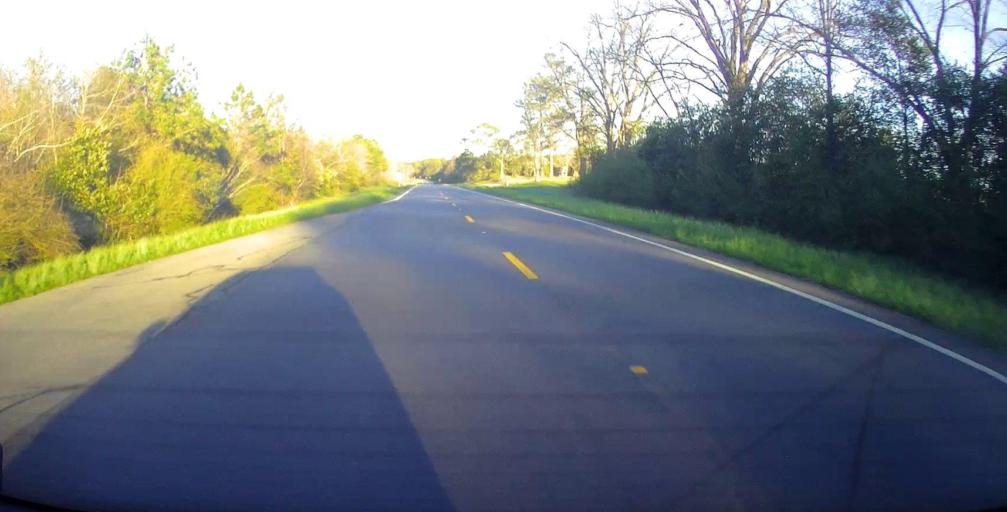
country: US
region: Georgia
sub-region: Wilcox County
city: Rochelle
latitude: 31.9453
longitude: -83.5232
